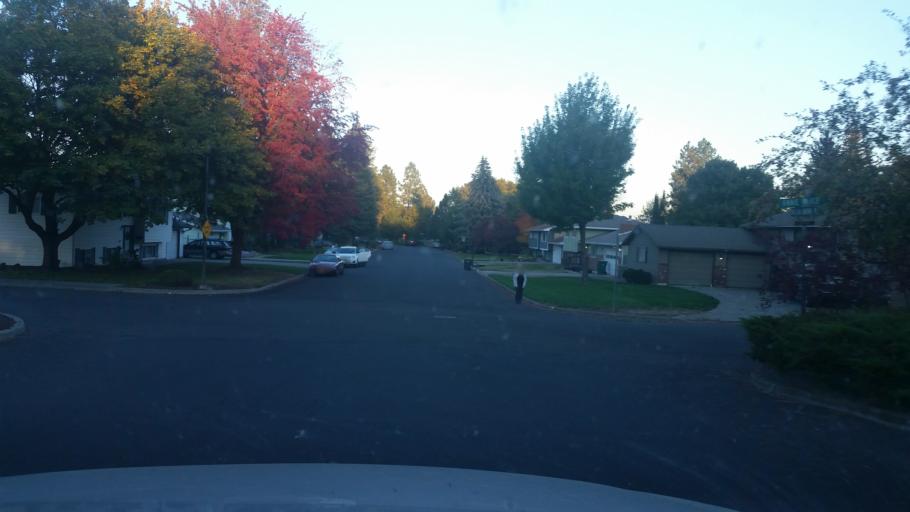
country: US
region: Washington
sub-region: Spokane County
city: Cheney
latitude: 47.4997
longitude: -117.5725
